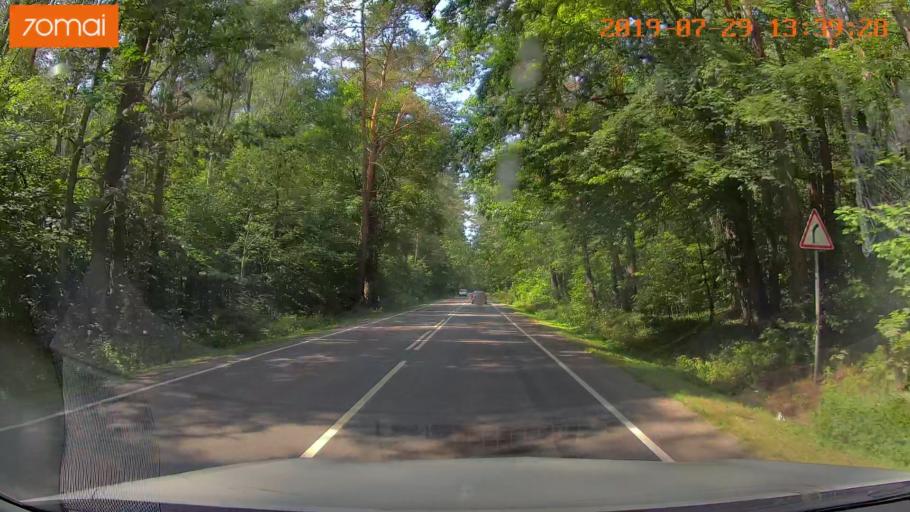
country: RU
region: Kaliningrad
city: Svetlyy
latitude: 54.7240
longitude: 20.1527
